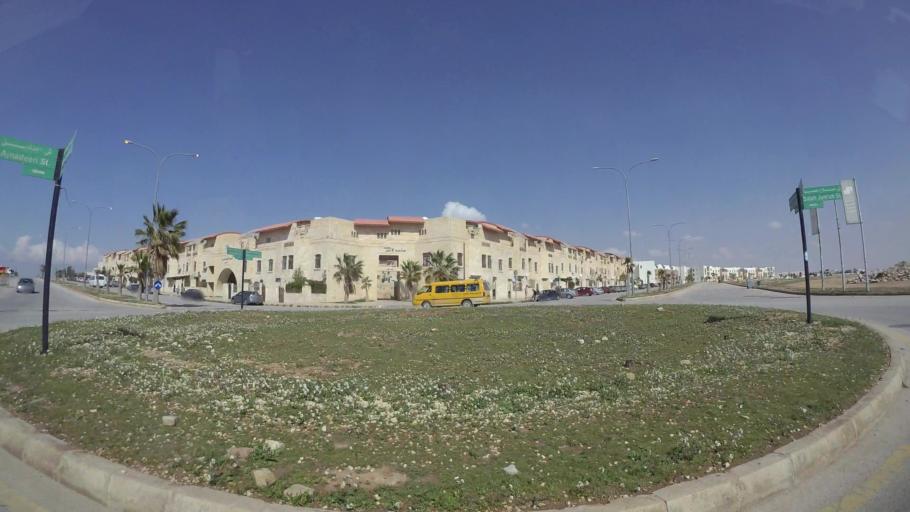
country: JO
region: Zarqa
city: Zarqa
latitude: 32.0710
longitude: 36.1072
